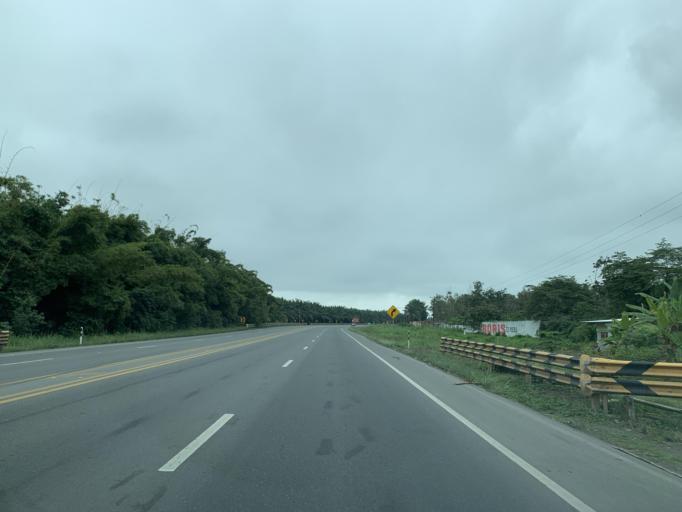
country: EC
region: Guayas
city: Coronel Marcelino Mariduena
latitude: -2.3253
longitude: -79.4495
